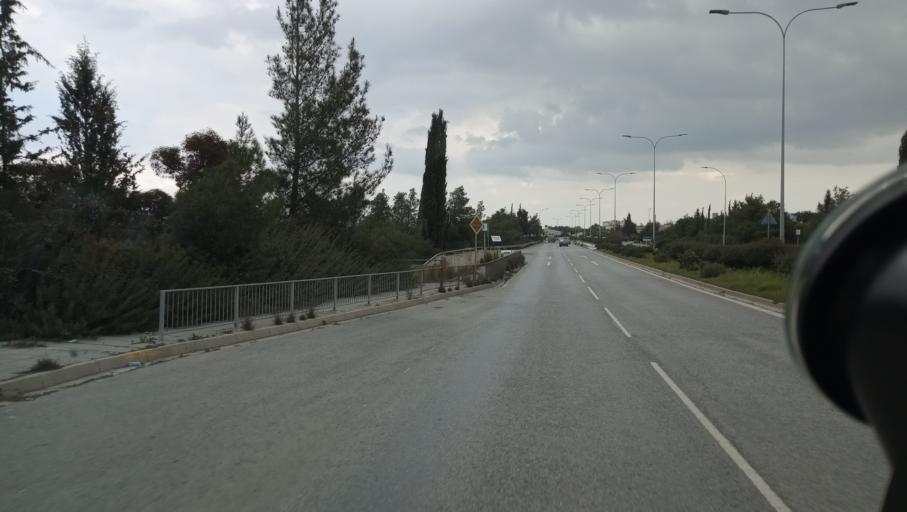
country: CY
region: Lefkosia
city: Kato Deftera
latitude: 35.1249
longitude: 33.2923
